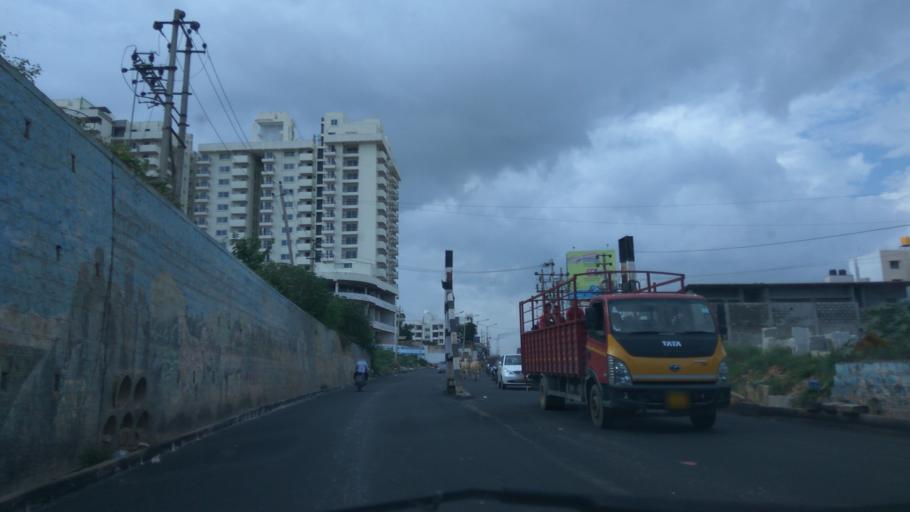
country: IN
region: Karnataka
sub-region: Bangalore Urban
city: Yelahanka
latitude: 13.0595
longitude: 77.6328
